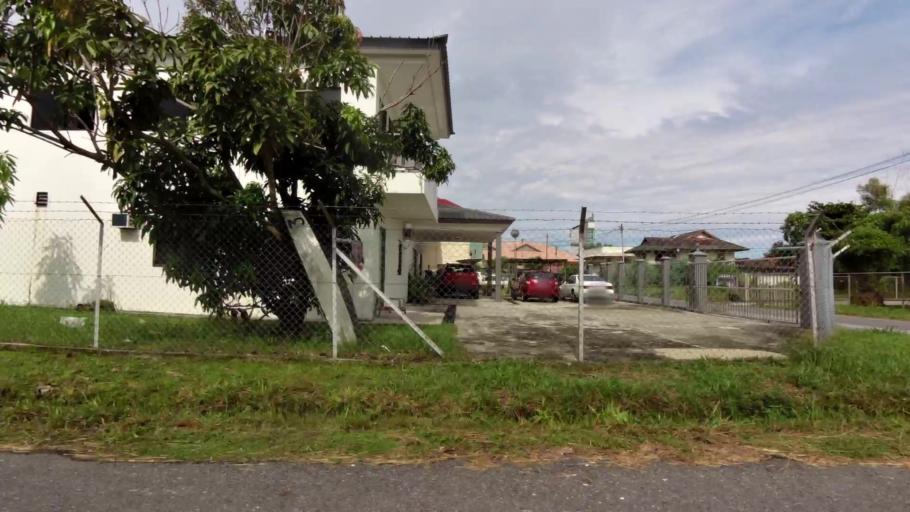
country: BN
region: Belait
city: Seria
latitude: 4.6147
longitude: 114.3324
